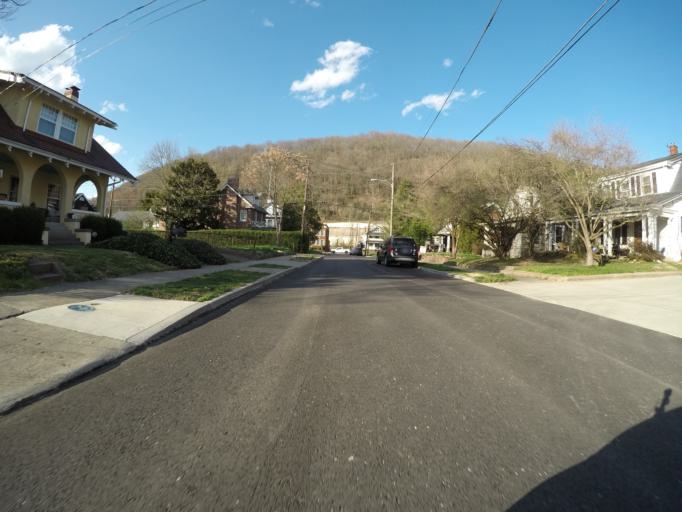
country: US
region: West Virginia
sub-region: Kanawha County
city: Charleston
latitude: 38.3355
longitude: -81.6063
